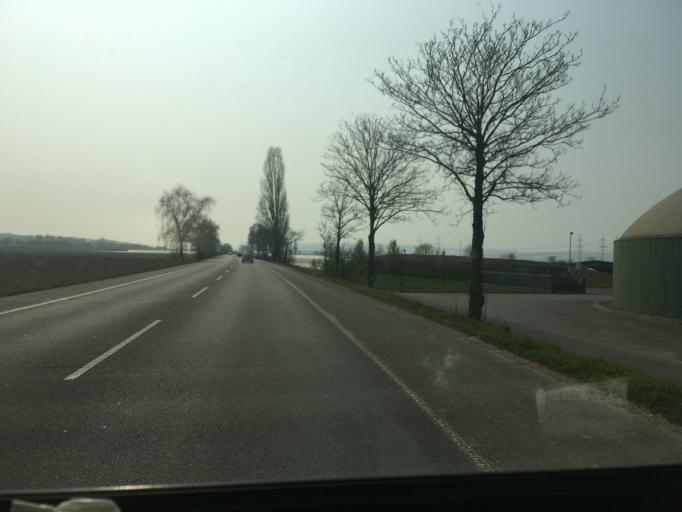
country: DE
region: North Rhine-Westphalia
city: Bornheim
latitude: 50.7949
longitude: 6.9908
